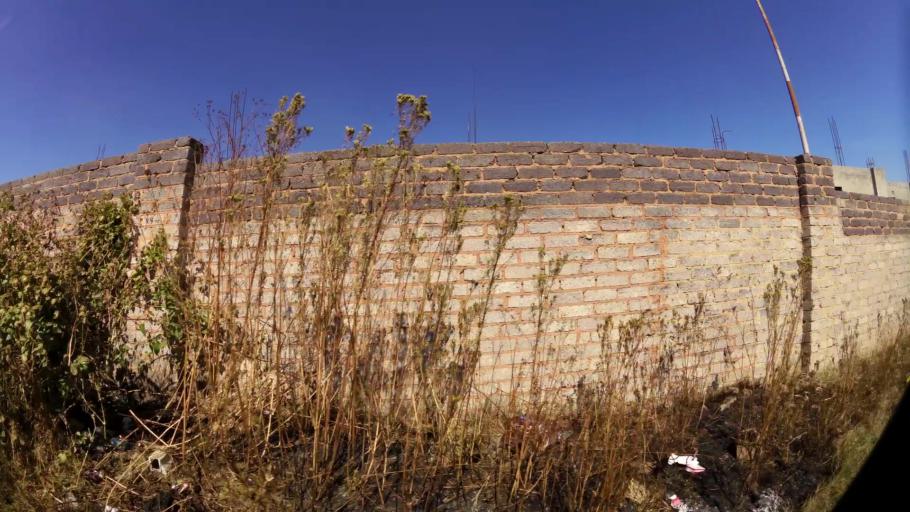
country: ZA
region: Gauteng
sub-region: City of Johannesburg Metropolitan Municipality
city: Soweto
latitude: -26.2381
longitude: 27.8927
